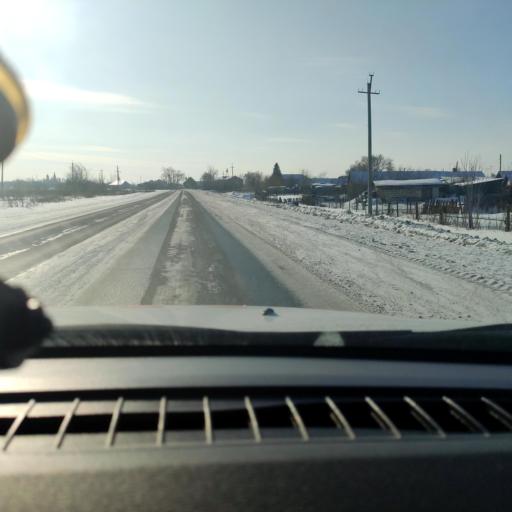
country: RU
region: Samara
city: Smyshlyayevka
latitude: 53.1815
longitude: 50.4670
